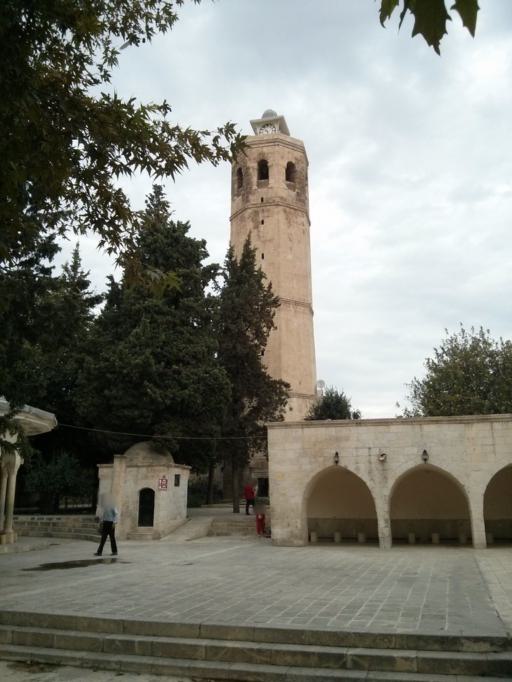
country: TR
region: Sanliurfa
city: Sanliurfa
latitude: 37.1515
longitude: 38.7900
